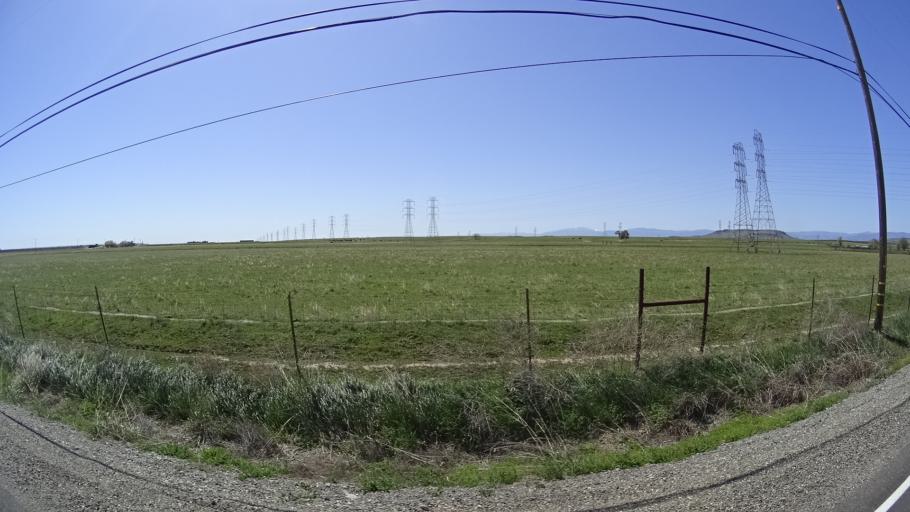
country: US
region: California
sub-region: Glenn County
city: Orland
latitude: 39.7721
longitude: -122.2637
